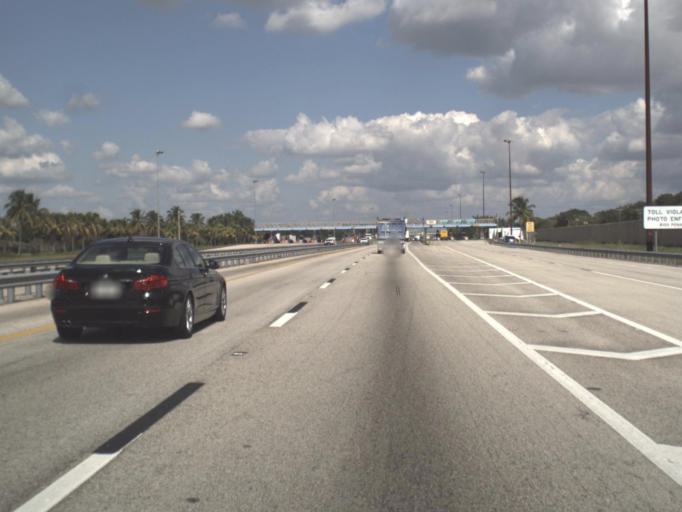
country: US
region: Florida
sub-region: Palm Beach County
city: Seminole Manor
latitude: 26.5597
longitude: -80.1730
